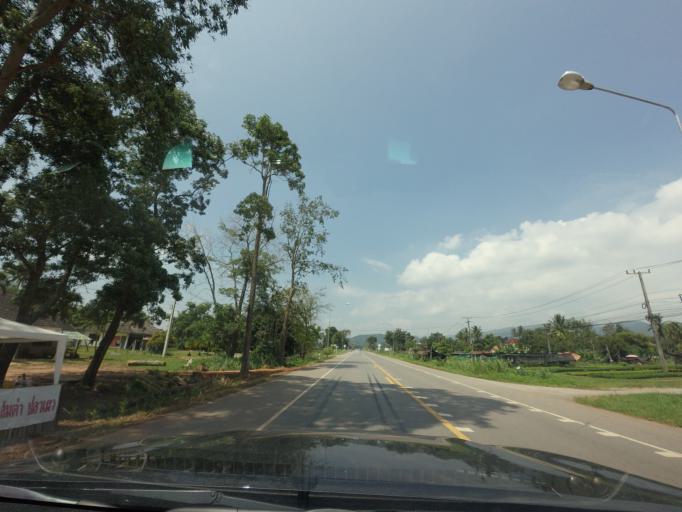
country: TH
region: Loei
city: Phu Ruea
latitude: 17.4563
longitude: 101.3935
